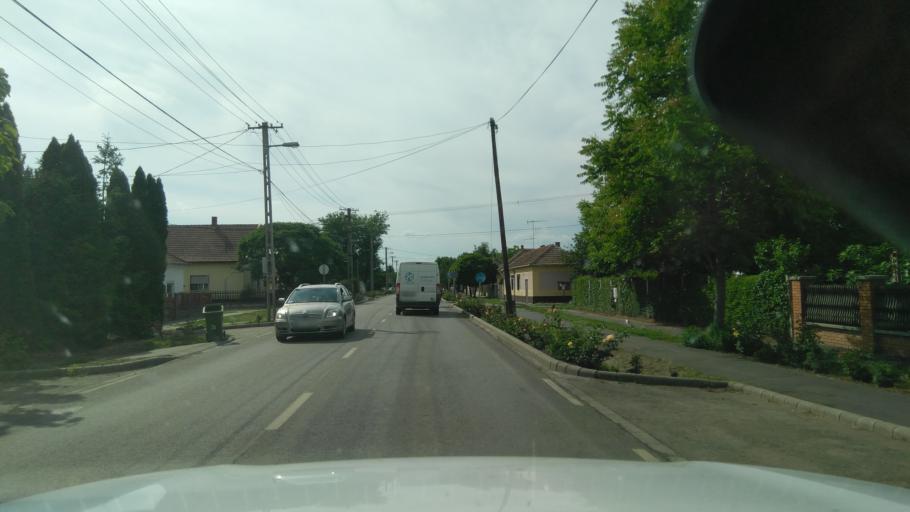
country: HU
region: Bekes
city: Medgyesegyhaza
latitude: 46.5015
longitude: 21.0209
